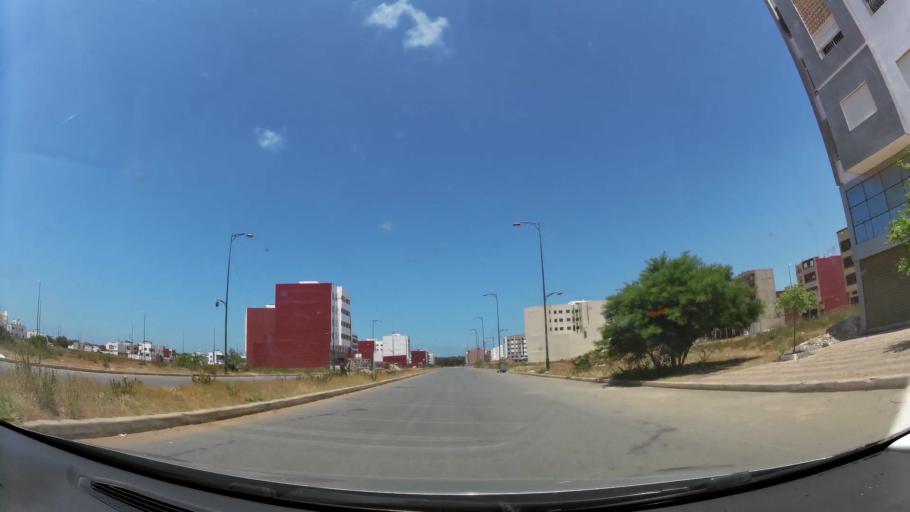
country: MA
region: Gharb-Chrarda-Beni Hssen
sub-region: Kenitra Province
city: Kenitra
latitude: 34.2656
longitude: -6.6262
